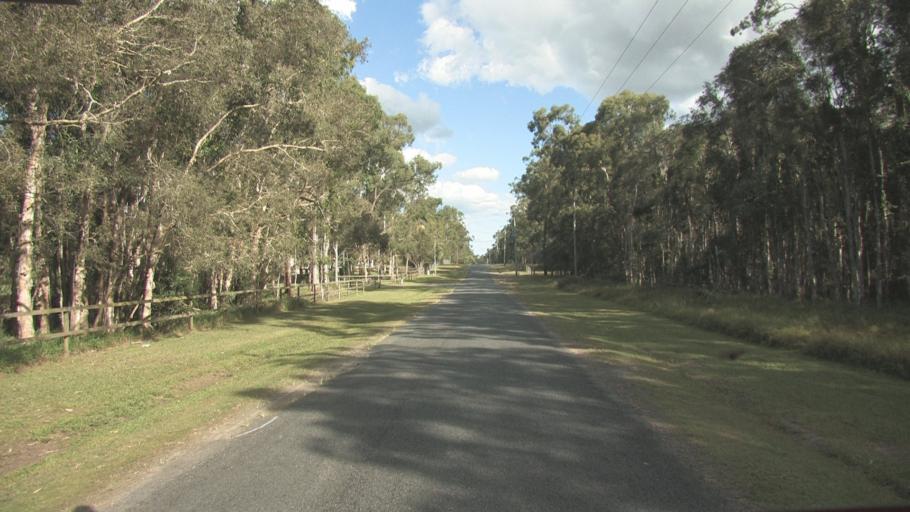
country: AU
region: Queensland
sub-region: Gold Coast
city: Yatala
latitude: -27.6633
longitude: 153.2410
